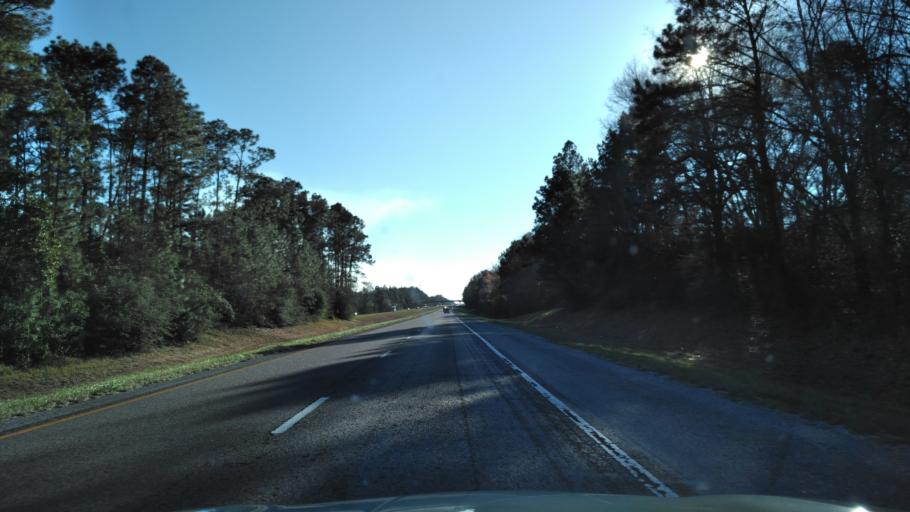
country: US
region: Alabama
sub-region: Baldwin County
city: Bay Minette
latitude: 31.0029
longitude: -87.6814
